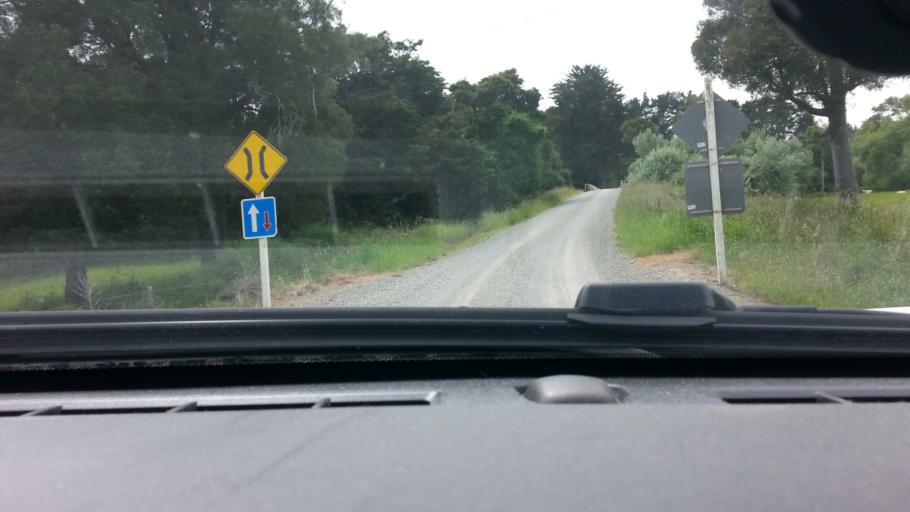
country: NZ
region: Wellington
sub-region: Masterton District
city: Masterton
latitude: -41.2129
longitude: 175.6778
